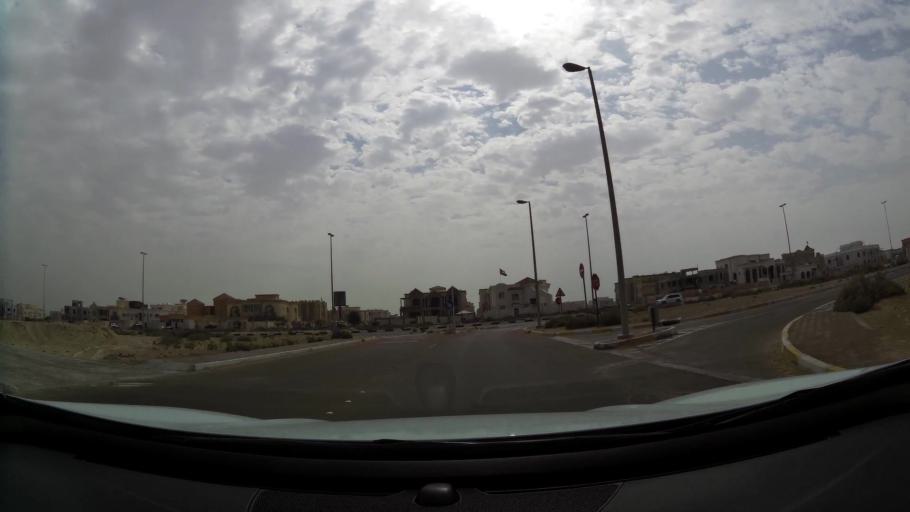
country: AE
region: Abu Dhabi
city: Abu Dhabi
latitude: 24.3143
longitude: 54.6457
